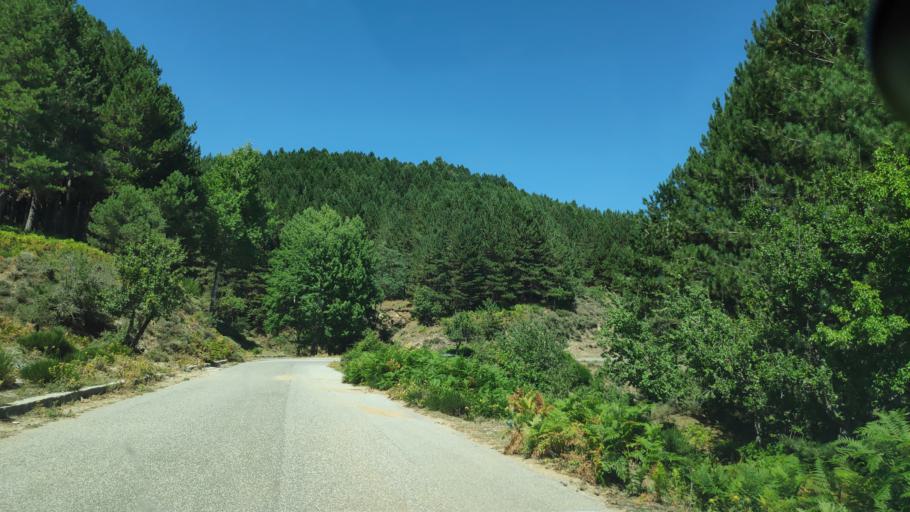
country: IT
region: Calabria
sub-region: Provincia di Reggio Calabria
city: Bova
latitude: 38.0324
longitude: 15.9459
